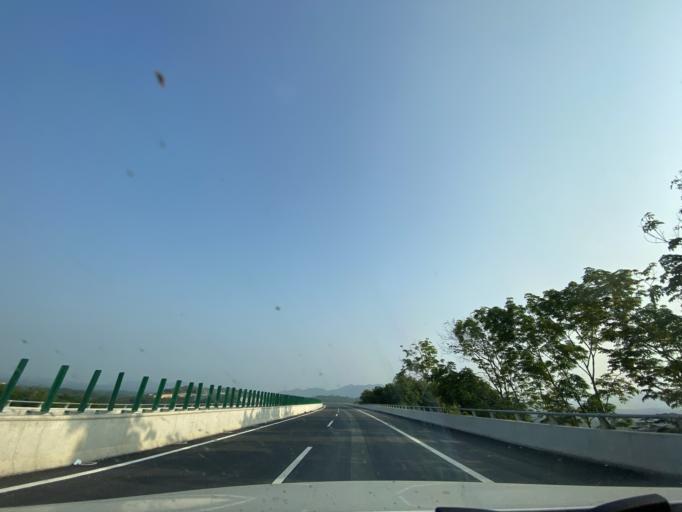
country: CN
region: Hainan
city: Xiangshui
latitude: 18.6385
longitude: 109.6297
